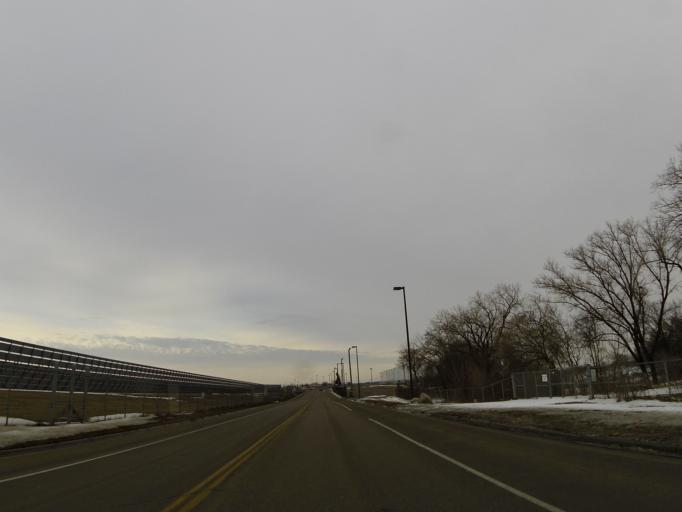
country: US
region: Minnesota
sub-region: Dakota County
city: Mendota Heights
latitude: 44.8730
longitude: -93.2063
